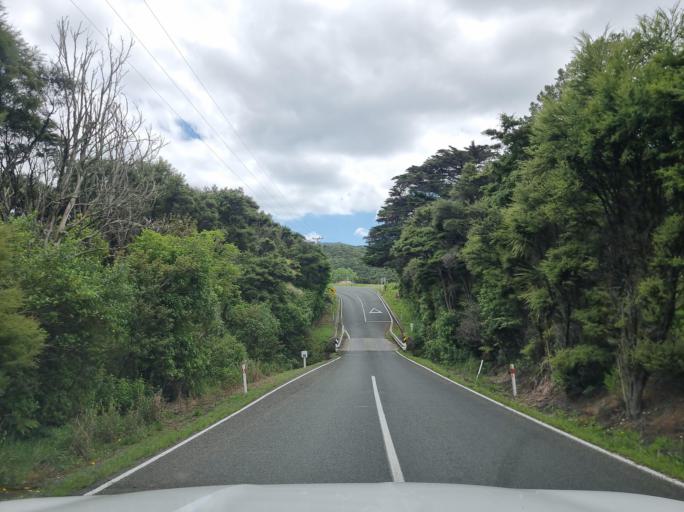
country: NZ
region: Auckland
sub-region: Auckland
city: Wellsford
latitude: -36.0875
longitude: 174.5352
